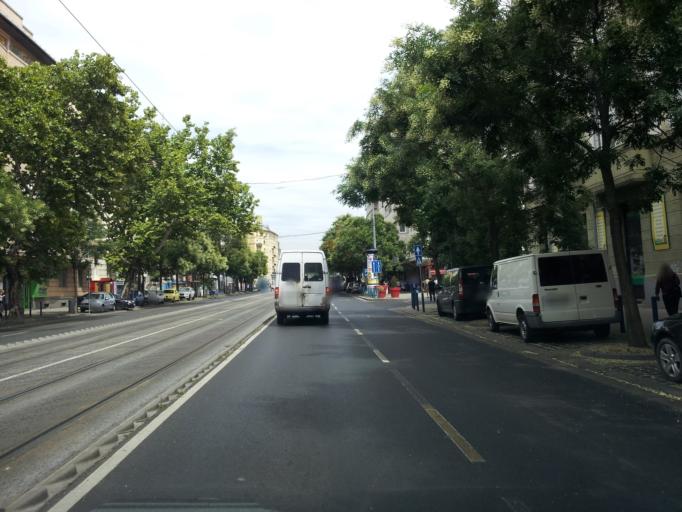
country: HU
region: Budapest
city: Budapest XI. keruelet
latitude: 47.4768
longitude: 19.0444
